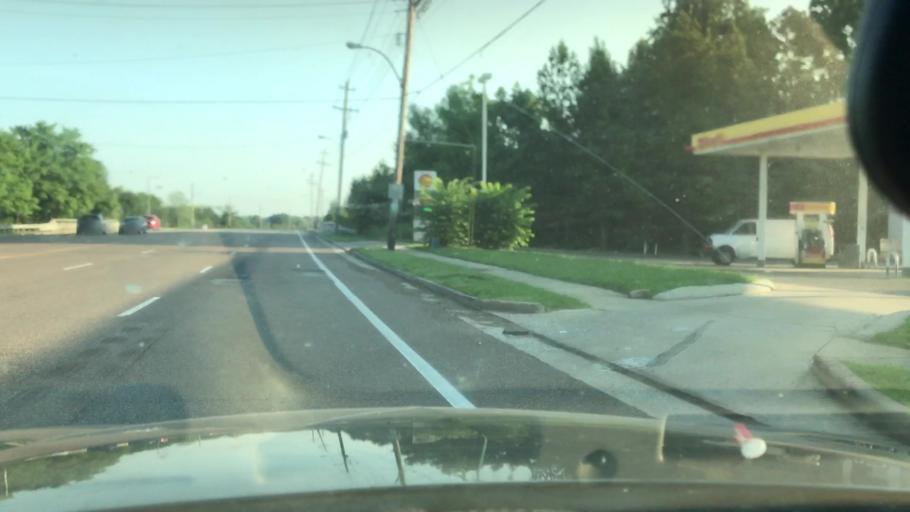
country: US
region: Tennessee
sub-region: Shelby County
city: Bartlett
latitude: 35.1892
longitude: -89.8141
